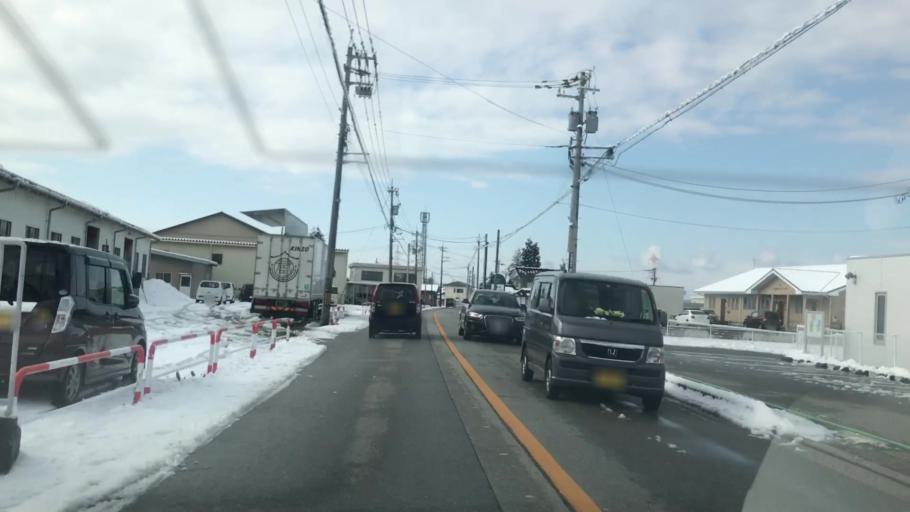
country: JP
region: Toyama
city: Toyama-shi
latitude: 36.6322
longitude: 137.2194
